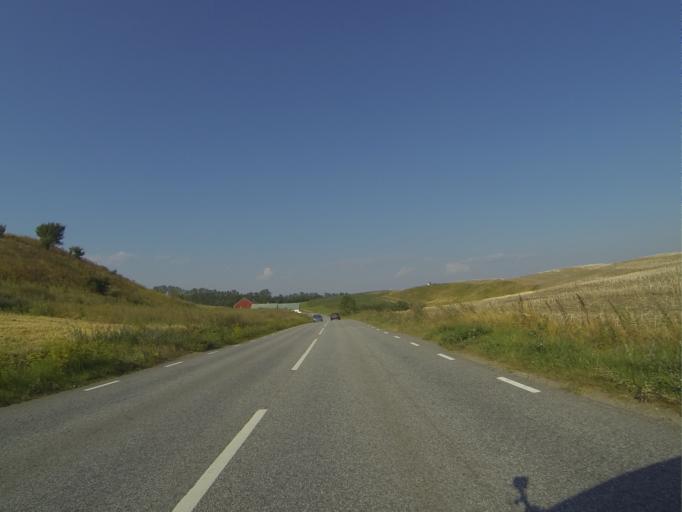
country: SE
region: Skane
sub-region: Svedala Kommun
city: Klagerup
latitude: 55.5884
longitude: 13.2213
